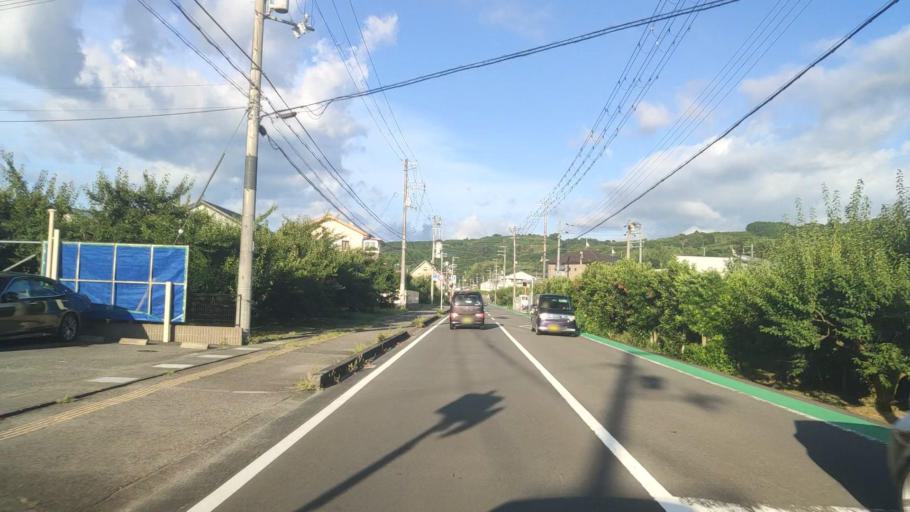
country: JP
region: Wakayama
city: Tanabe
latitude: 33.7347
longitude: 135.4222
